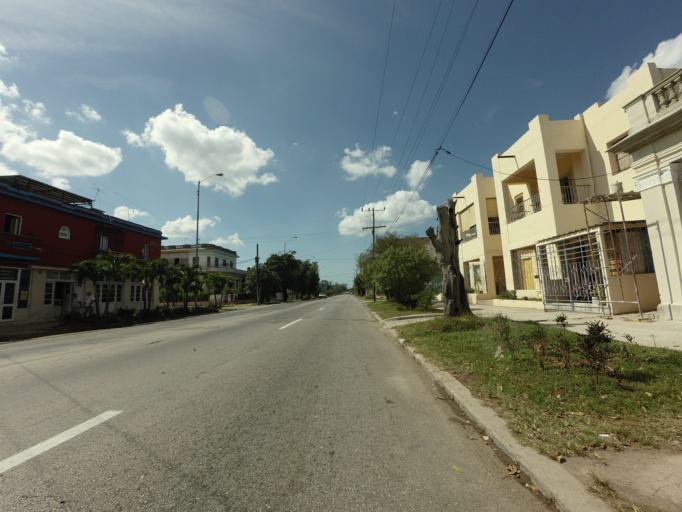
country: CU
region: La Habana
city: Cerro
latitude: 23.1123
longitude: -82.4196
